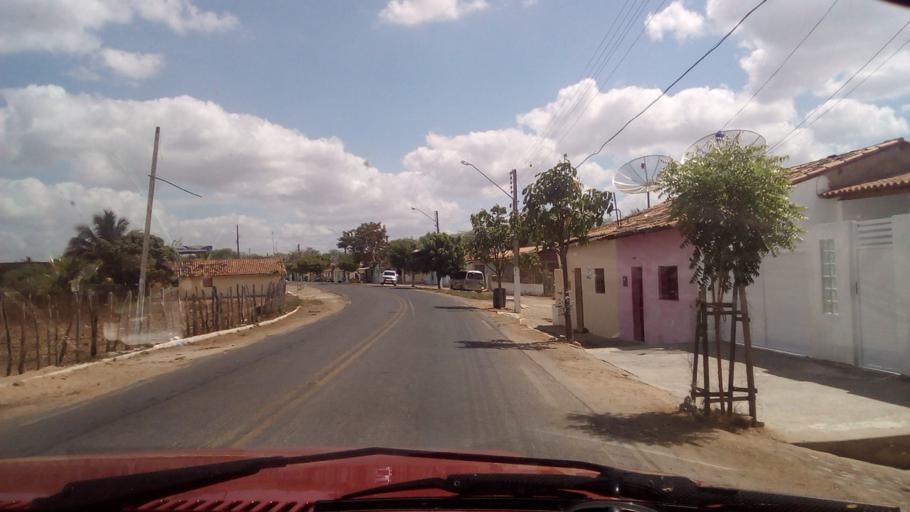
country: BR
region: Paraiba
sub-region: Dona Ines
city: Dona Ines
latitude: -6.5378
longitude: -35.6551
